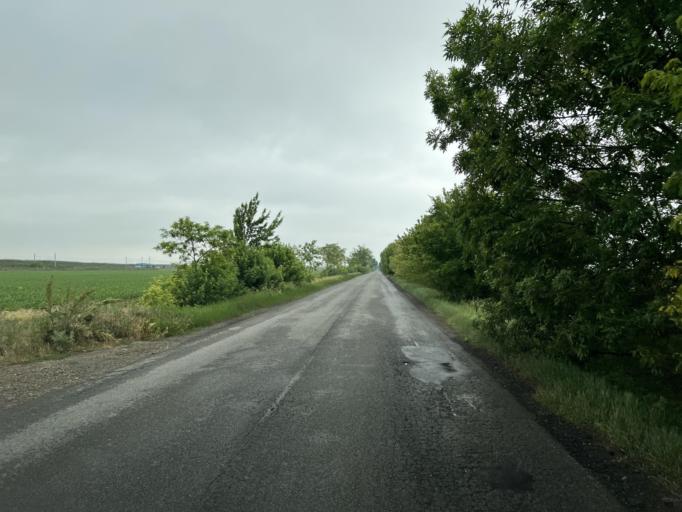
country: HU
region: Pest
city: Tura
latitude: 47.6276
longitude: 19.6239
